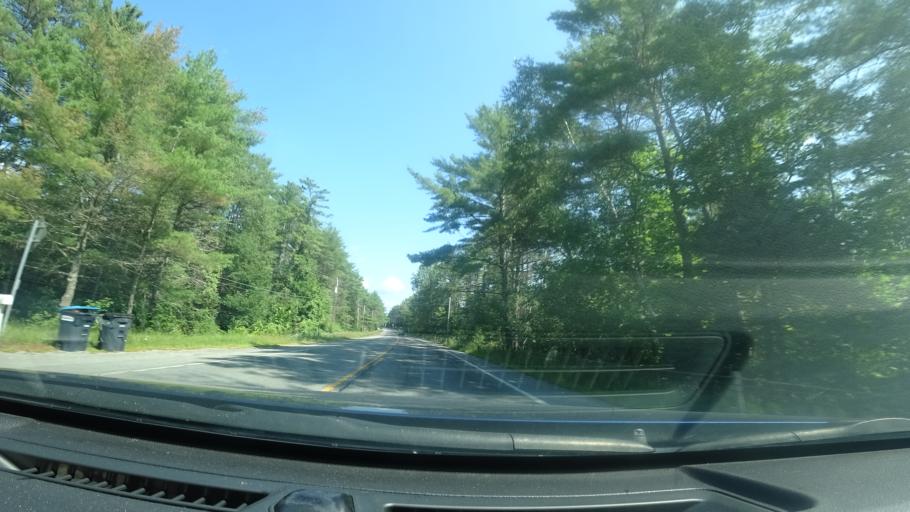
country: US
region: New York
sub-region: Warren County
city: Warrensburg
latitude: 43.6376
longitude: -73.7978
